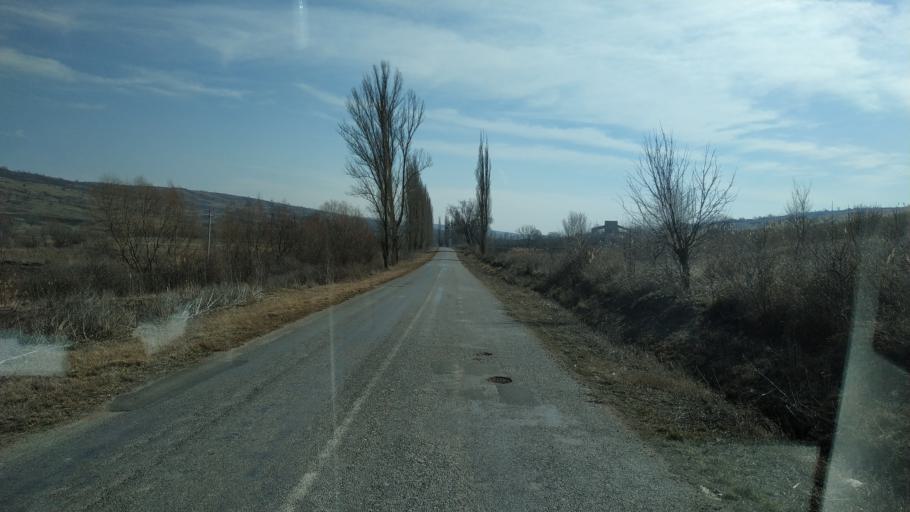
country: MD
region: Nisporeni
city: Nisporeni
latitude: 47.1649
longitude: 28.1002
